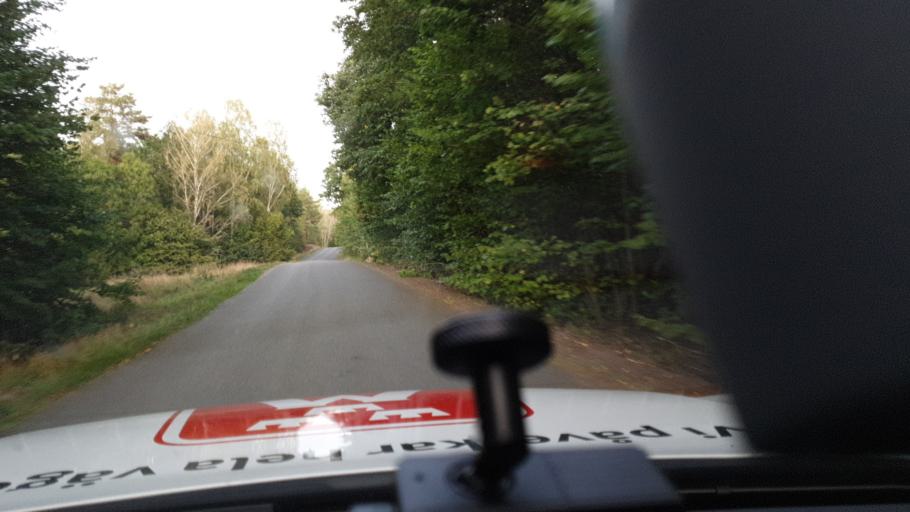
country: SE
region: Kalmar
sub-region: Hogsby Kommun
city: Hoegsby
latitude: 57.0818
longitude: 16.0263
